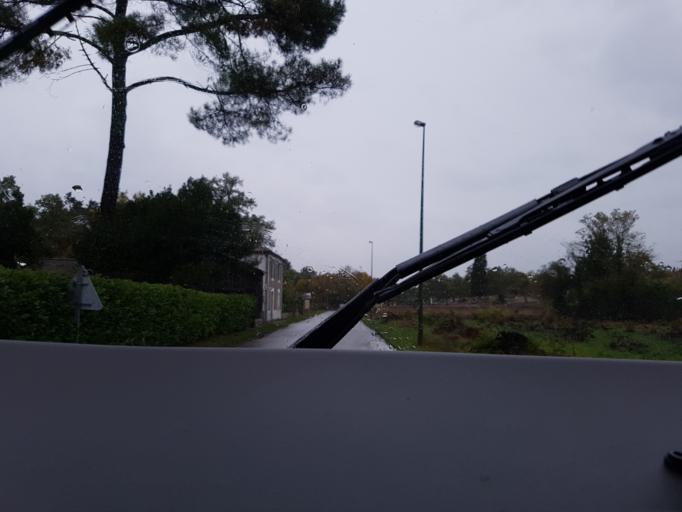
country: FR
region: Aquitaine
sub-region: Departement de la Gironde
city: Saint-Symphorien
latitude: 44.3251
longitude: -0.5833
